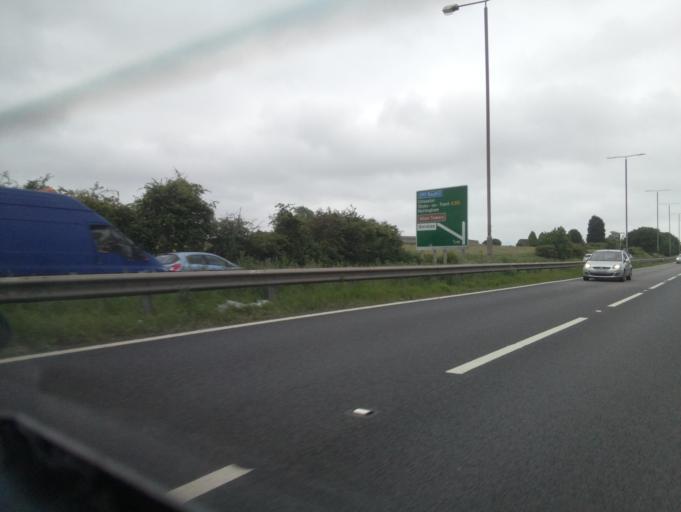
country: GB
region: England
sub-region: Derbyshire
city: Findern
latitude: 52.8767
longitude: -1.5547
